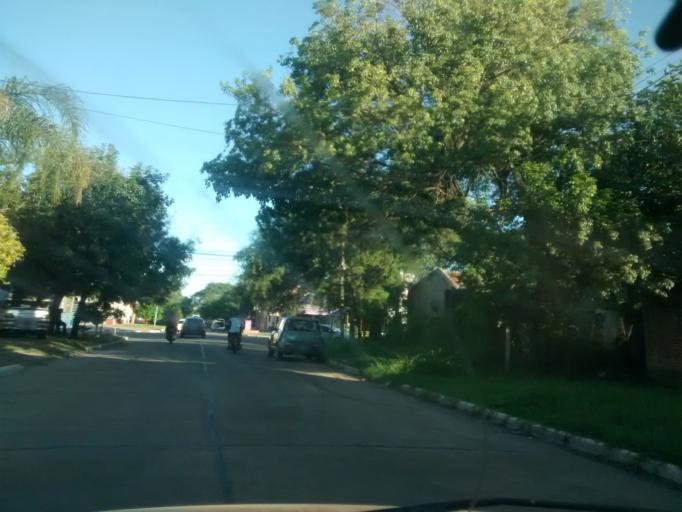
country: AR
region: Chaco
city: Resistencia
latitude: -27.4634
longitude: -58.9923
